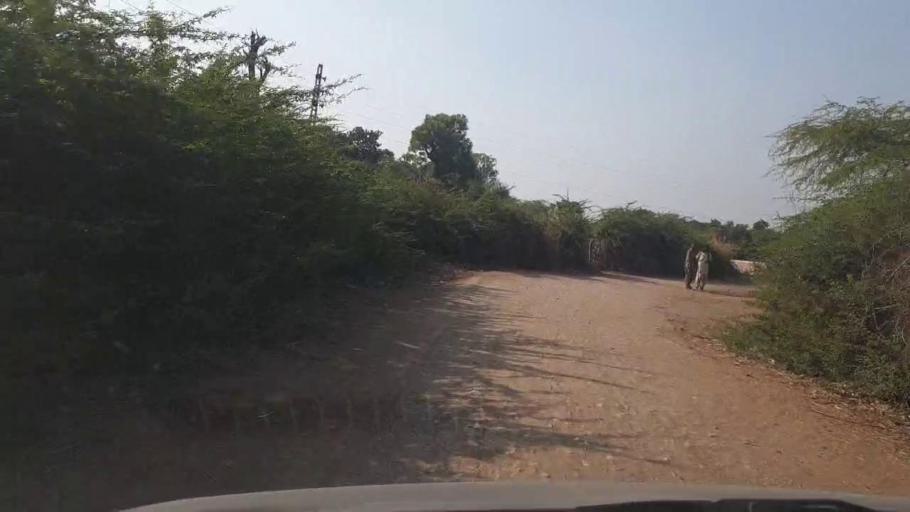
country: PK
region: Sindh
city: Digri
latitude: 25.2539
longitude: 69.1475
